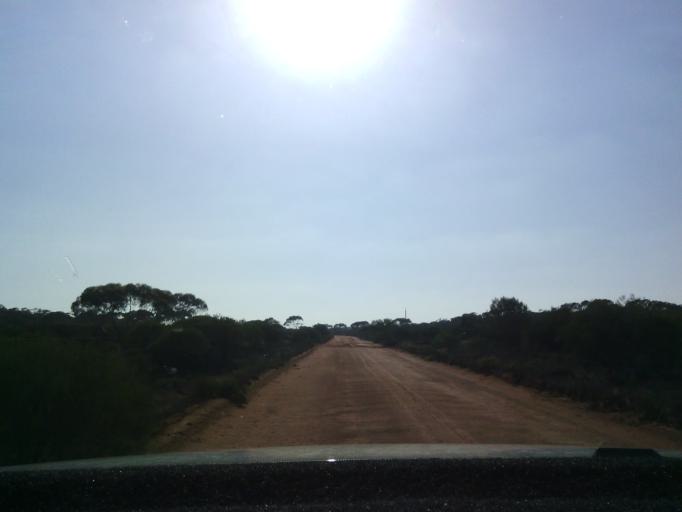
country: AU
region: South Australia
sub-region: Berri and Barmera
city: Monash
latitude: -34.2250
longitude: 140.5845
